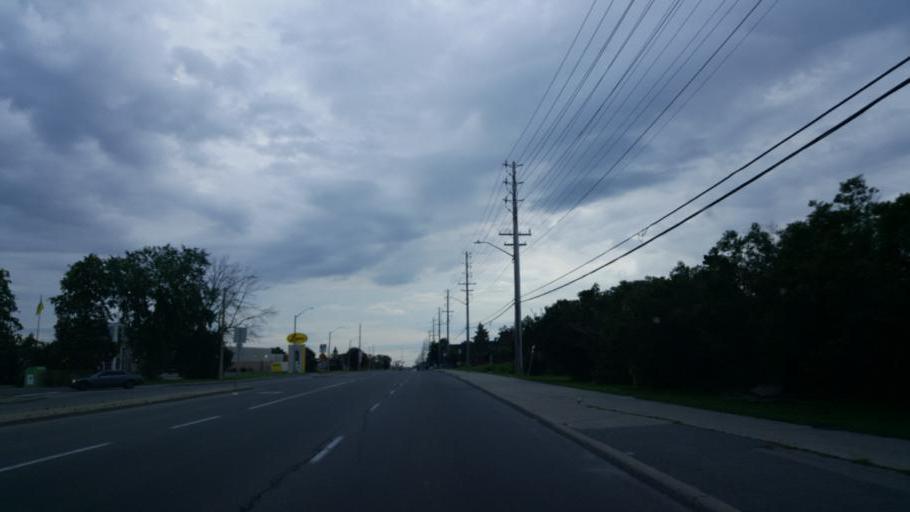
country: CA
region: Ontario
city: Ottawa
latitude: 45.3785
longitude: -75.6432
